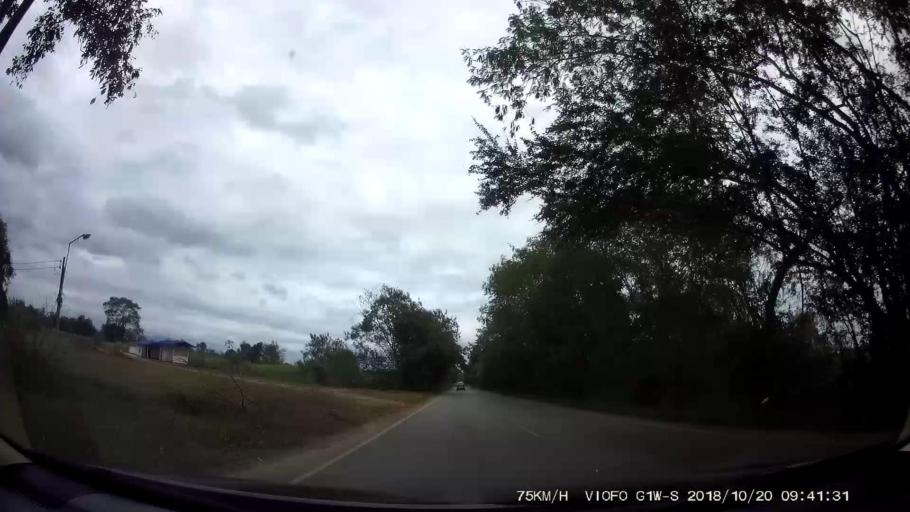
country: TH
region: Chaiyaphum
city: Khon San
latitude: 16.4541
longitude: 101.9566
